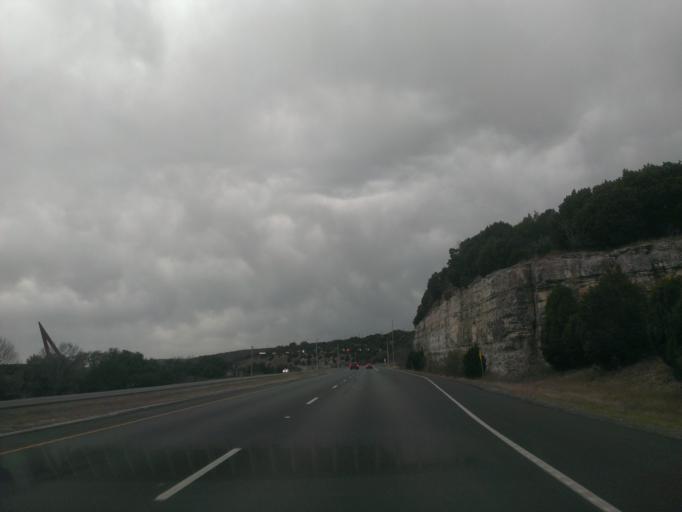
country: US
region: Texas
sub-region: Williamson County
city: Jollyville
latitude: 30.3883
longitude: -97.7577
